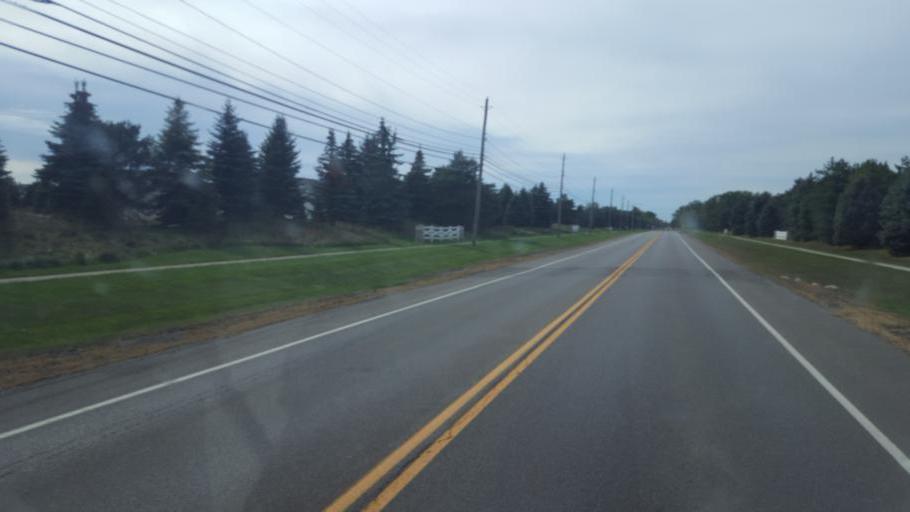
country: US
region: Ohio
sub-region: Lorain County
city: Avon Lake
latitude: 41.4933
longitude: -82.0356
